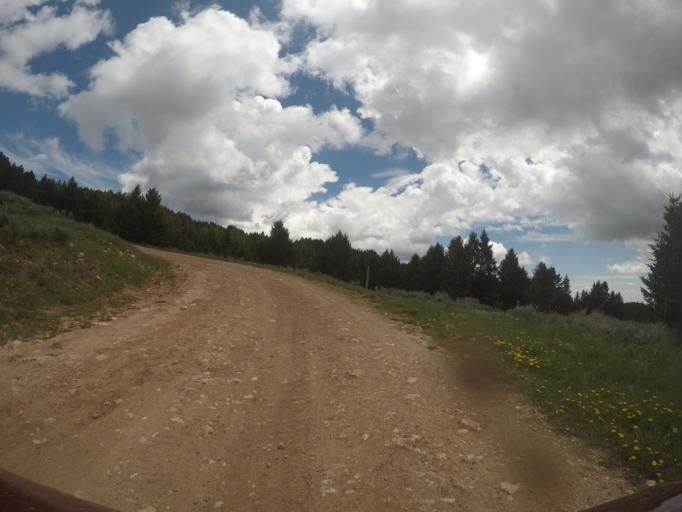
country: US
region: Wyoming
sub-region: Big Horn County
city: Lovell
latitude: 45.1682
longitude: -108.4240
